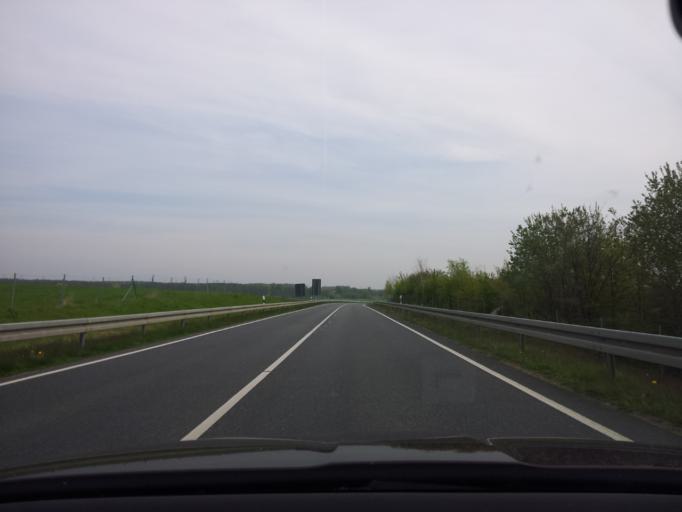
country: DE
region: Brandenburg
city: Luckau
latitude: 51.8573
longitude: 13.6882
